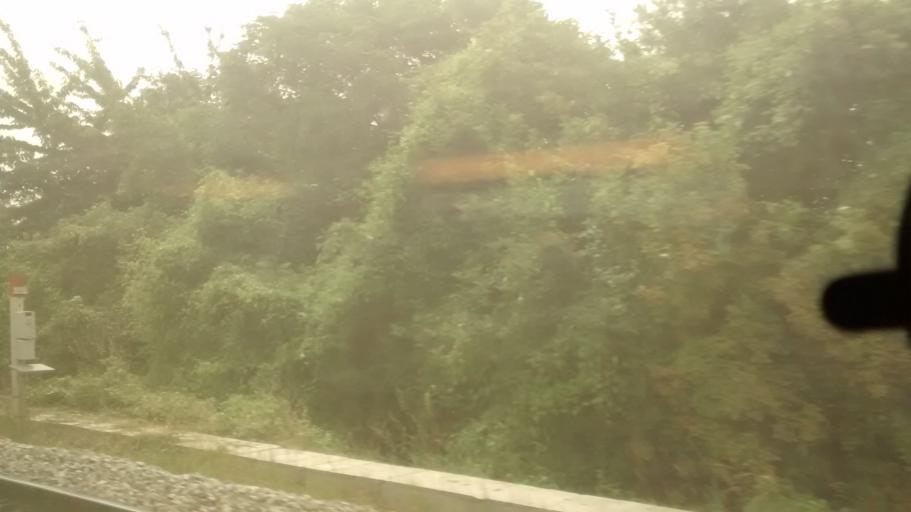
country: FR
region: Ile-de-France
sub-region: Departement du Val-de-Marne
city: Villeneuve-le-Roi
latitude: 48.7391
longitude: 2.4103
